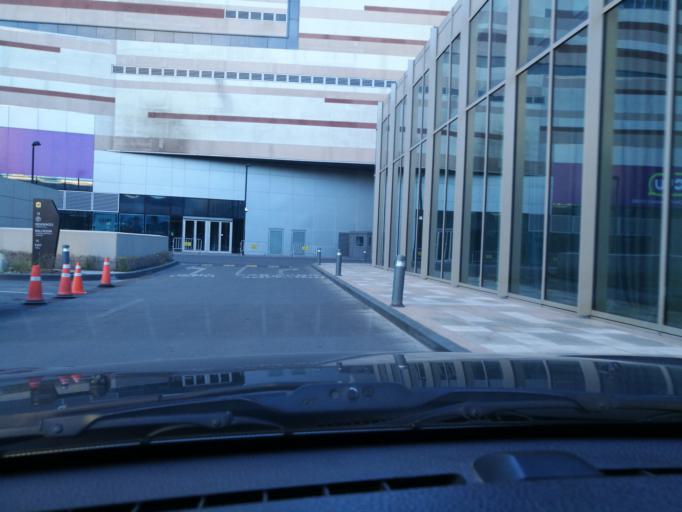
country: MN
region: Ulaanbaatar
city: Ulaanbaatar
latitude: 47.9132
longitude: 106.9208
